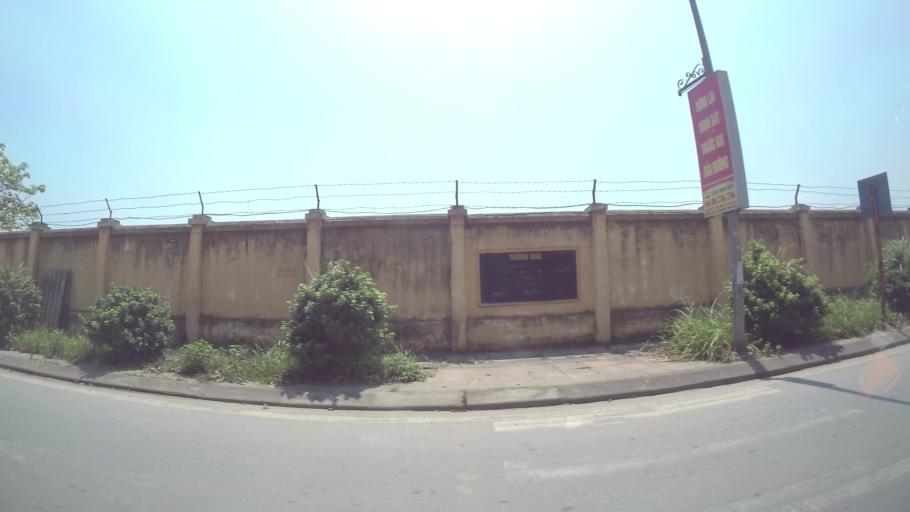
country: VN
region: Ha Noi
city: Hoan Kiem
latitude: 21.0492
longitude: 105.8892
